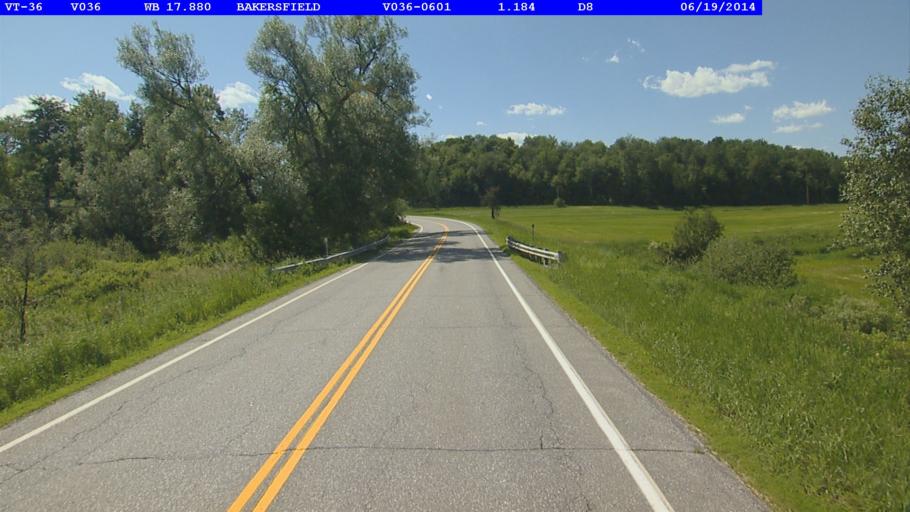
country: US
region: Vermont
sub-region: Franklin County
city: Enosburg Falls
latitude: 44.7829
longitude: -72.8270
